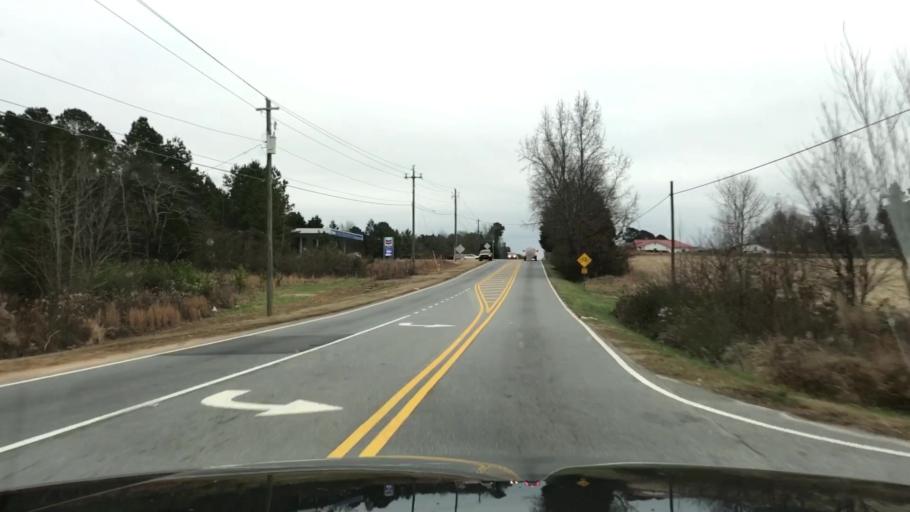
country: US
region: Georgia
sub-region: Gwinnett County
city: Dacula
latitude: 33.9723
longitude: -83.8905
